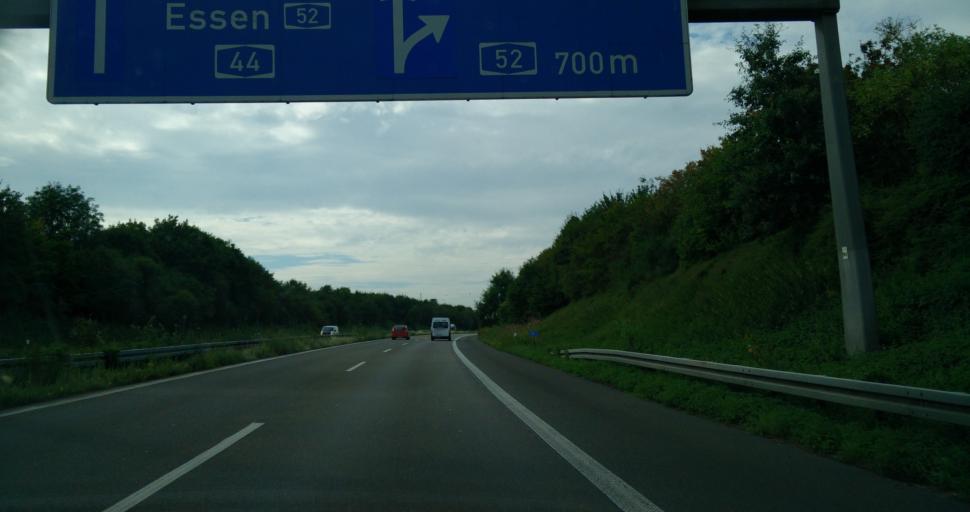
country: DE
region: North Rhine-Westphalia
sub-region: Regierungsbezirk Dusseldorf
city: Ratingen
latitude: 51.2743
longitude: 6.8194
